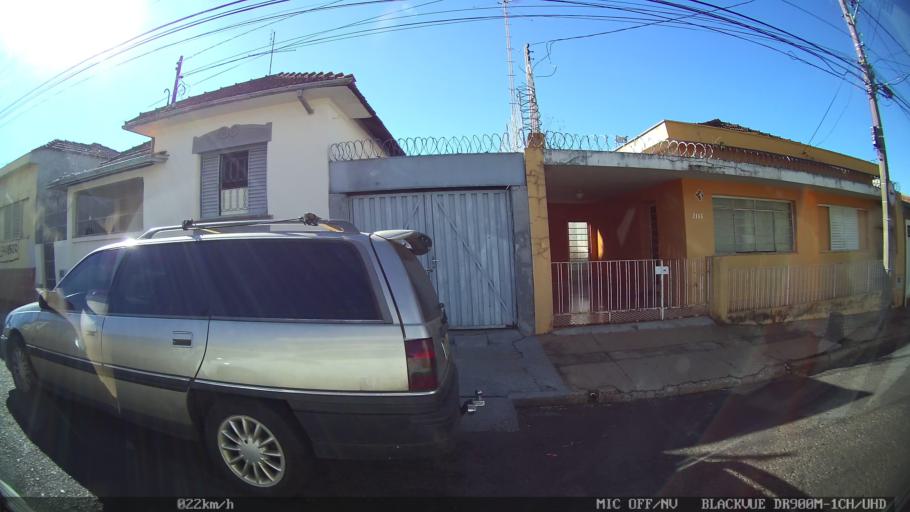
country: BR
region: Sao Paulo
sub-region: Franca
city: Franca
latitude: -20.5337
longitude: -47.4083
